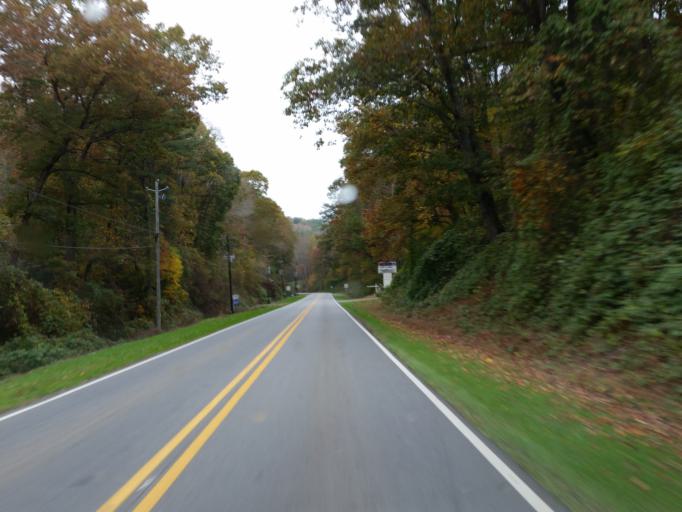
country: US
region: Georgia
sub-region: Pickens County
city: Jasper
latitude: 34.4746
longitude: -84.4225
